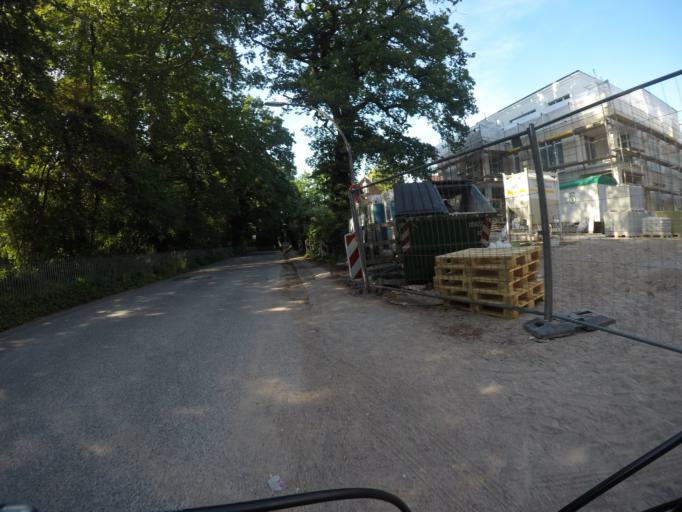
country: DE
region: Hamburg
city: Altona
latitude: 53.5532
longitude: 9.8731
